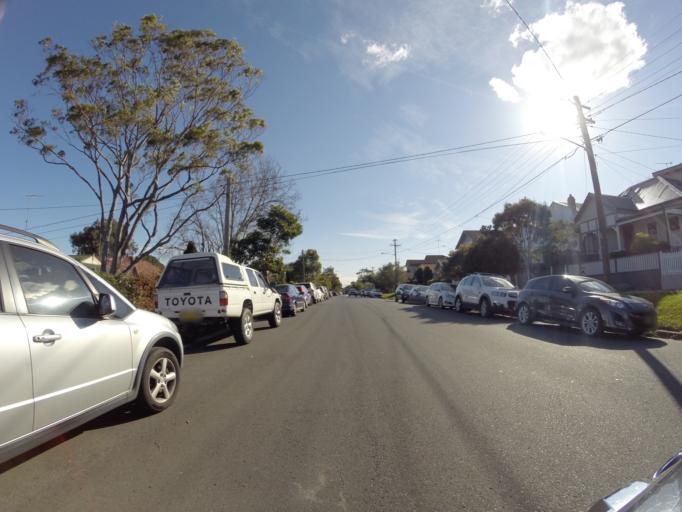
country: AU
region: New South Wales
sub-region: Randwick
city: Coogee
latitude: -33.9264
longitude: 151.2446
